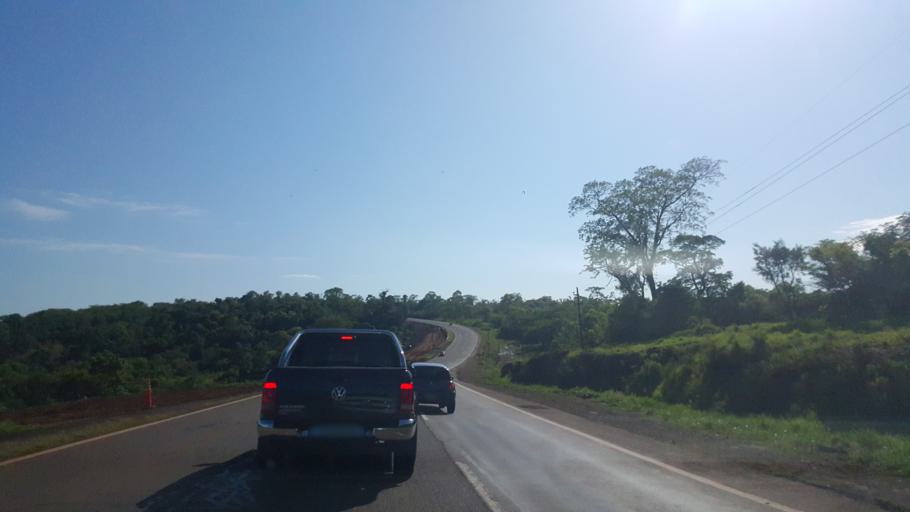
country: AR
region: Misiones
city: Santa Ana
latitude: -27.3547
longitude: -55.5535
